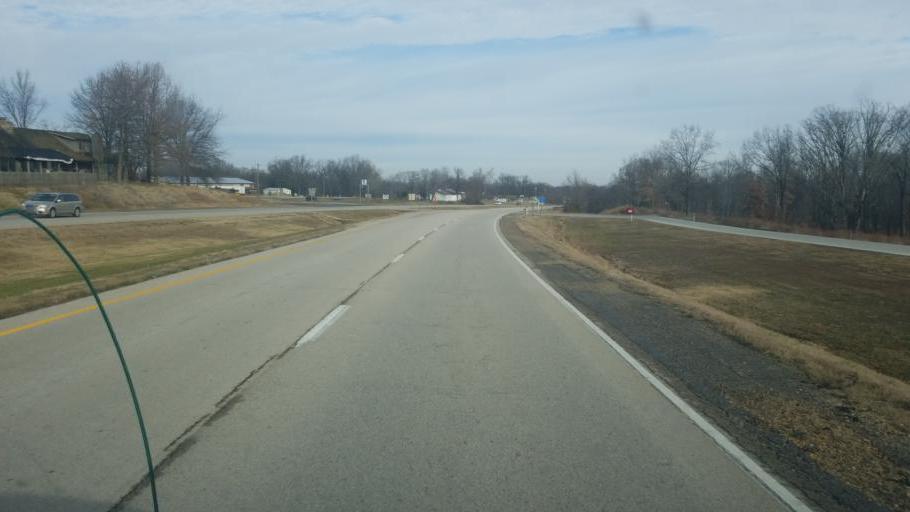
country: US
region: Missouri
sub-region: Stoddard County
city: Bloomfield
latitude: 36.8710
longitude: -89.9295
